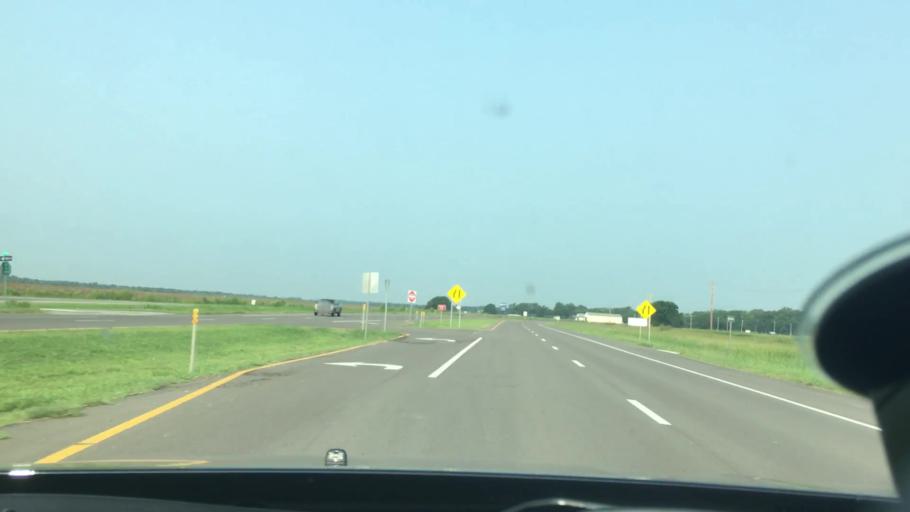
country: US
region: Oklahoma
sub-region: Garvin County
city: Pauls Valley
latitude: 34.7402
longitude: -97.2698
